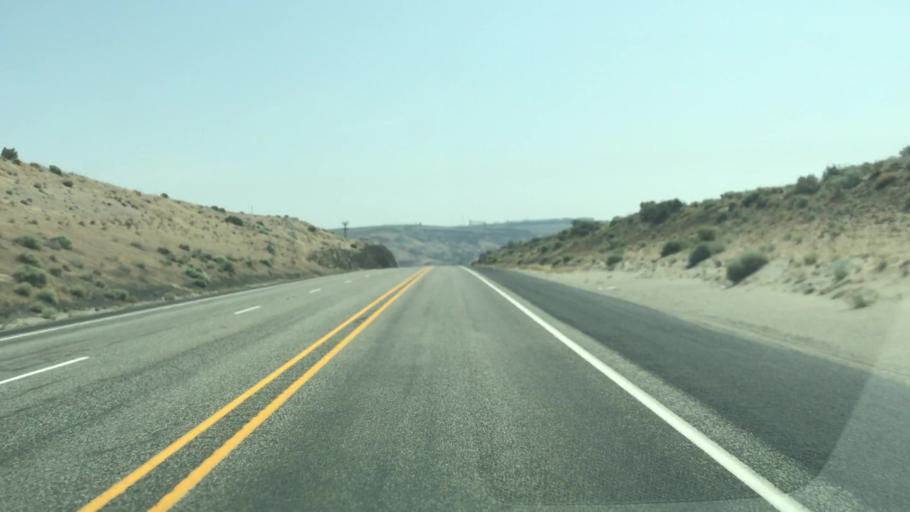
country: US
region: Washington
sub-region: Grant County
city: Quincy
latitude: 47.2337
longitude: -120.0190
